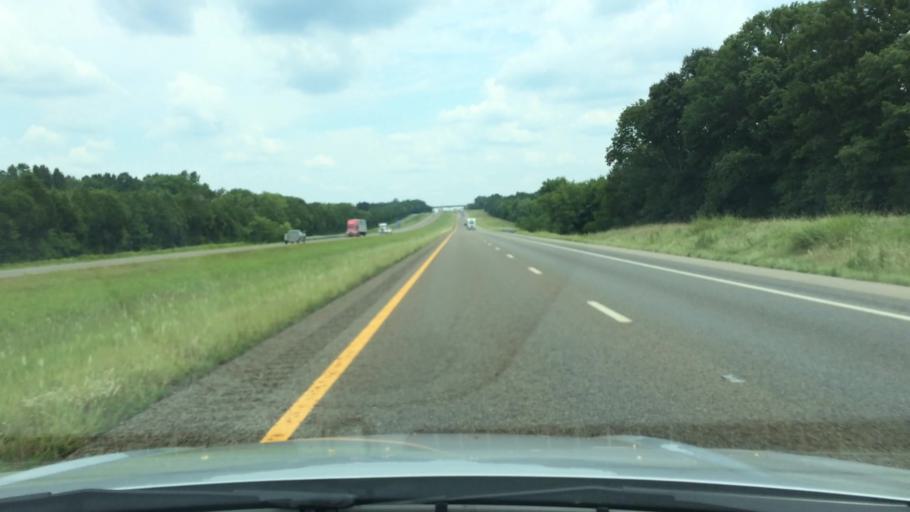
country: US
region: Tennessee
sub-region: Maury County
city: Columbia
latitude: 35.5796
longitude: -86.9040
